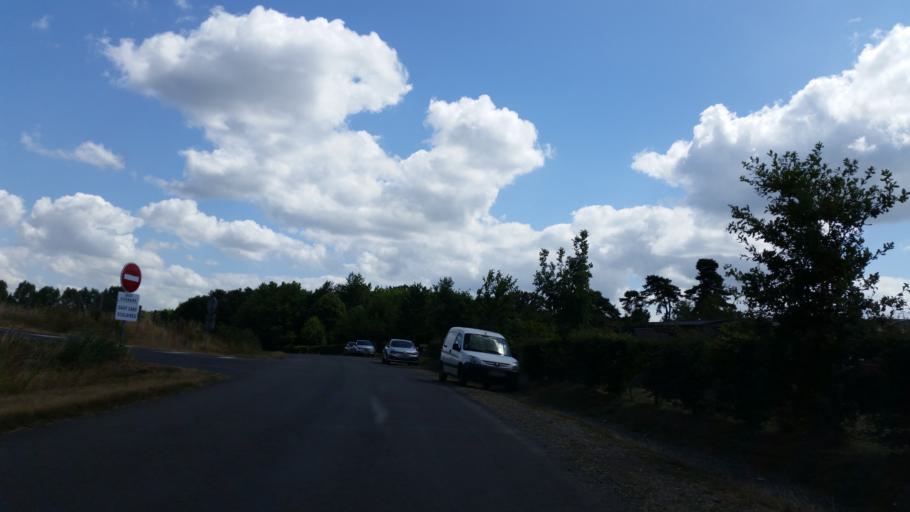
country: FR
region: Lower Normandy
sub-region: Departement de l'Orne
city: Briouze
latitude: 48.8293
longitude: -0.3810
